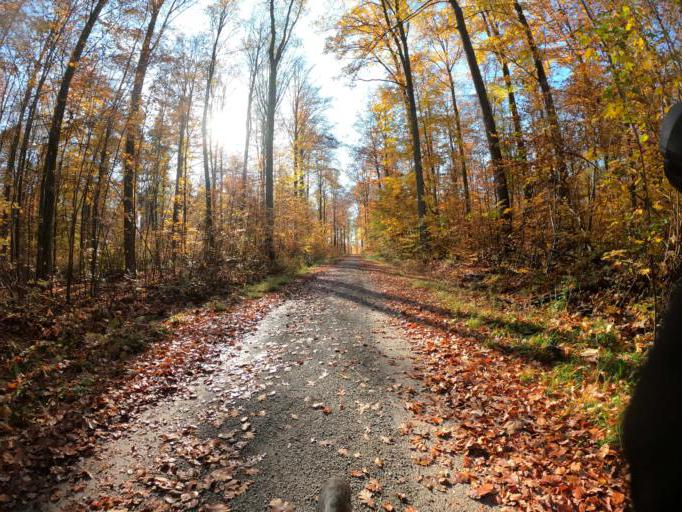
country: DE
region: Baden-Wuerttemberg
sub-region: Regierungsbezirk Stuttgart
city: Magstadt
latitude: 48.7537
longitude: 8.9832
